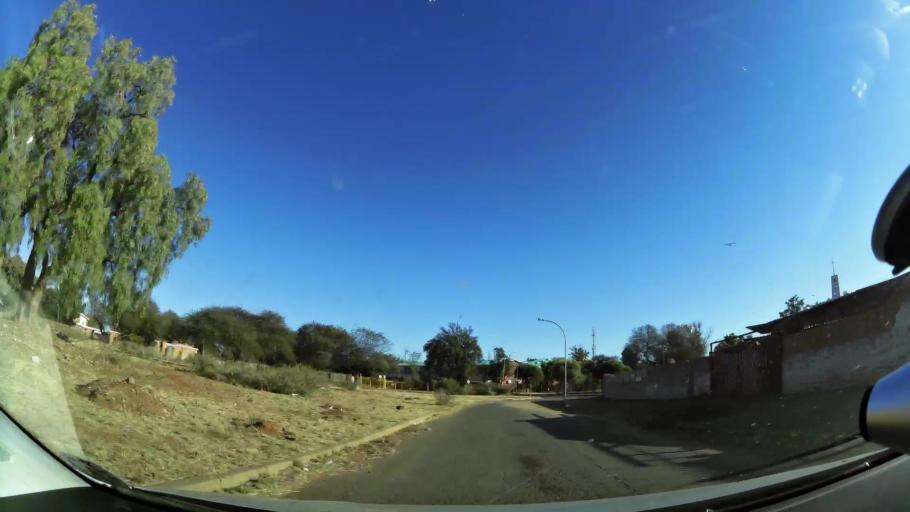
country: ZA
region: Northern Cape
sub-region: Frances Baard District Municipality
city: Kimberley
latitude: -28.7378
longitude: 24.7383
